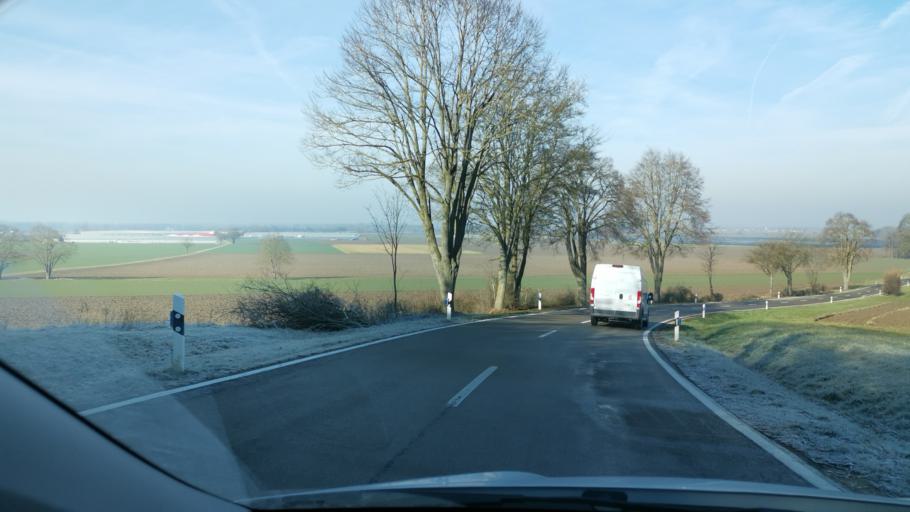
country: DE
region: Bavaria
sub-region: Swabia
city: Holzheim
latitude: 48.6263
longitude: 10.9297
